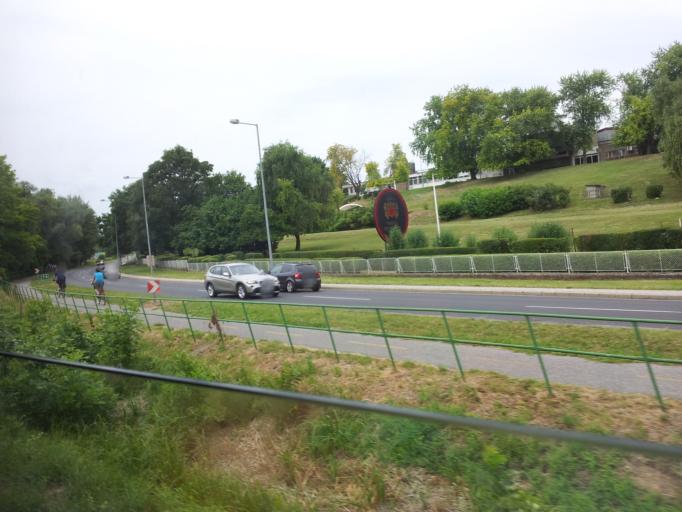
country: HU
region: Veszprem
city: Badacsonytomaj
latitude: 46.8043
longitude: 17.5359
